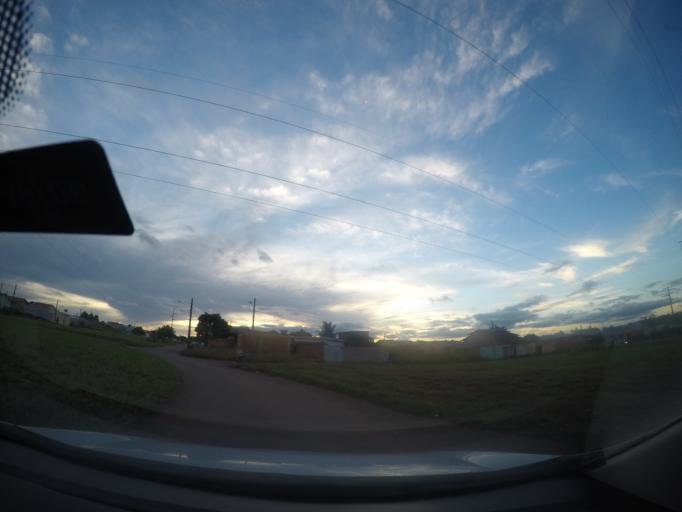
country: BR
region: Goias
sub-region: Goianira
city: Goianira
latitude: -16.5709
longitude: -49.3827
